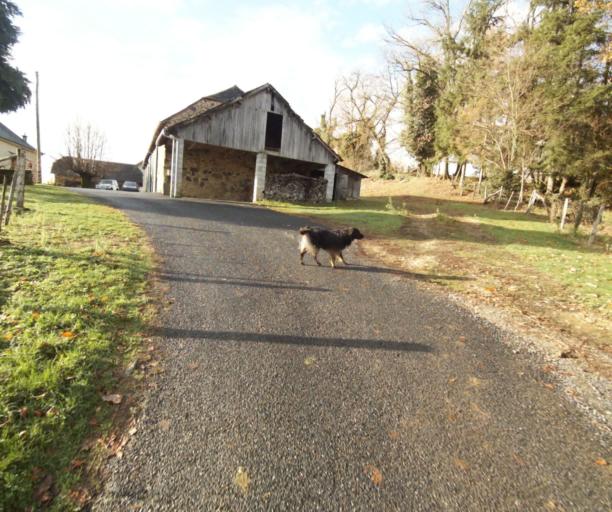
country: FR
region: Limousin
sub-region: Departement de la Correze
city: Sainte-Fereole
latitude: 45.2530
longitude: 1.6037
